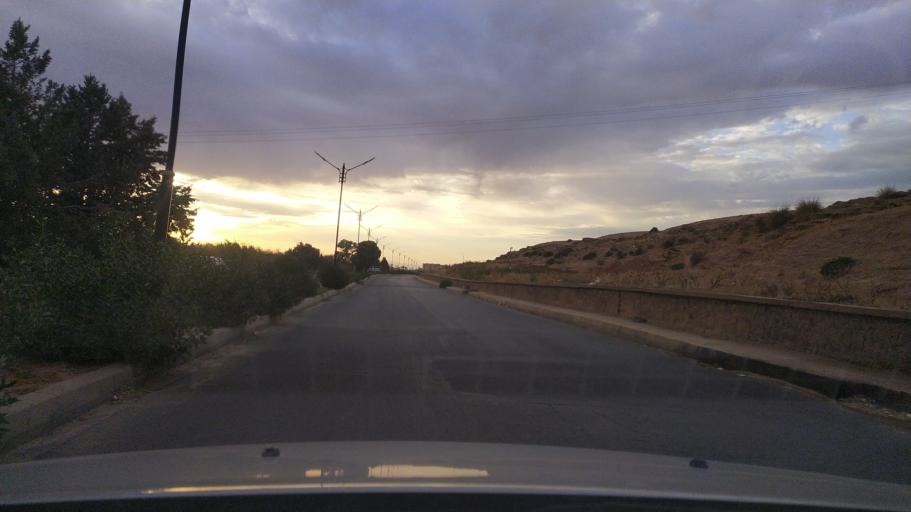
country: DZ
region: Tiaret
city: Frenda
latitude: 35.0512
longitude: 1.0724
